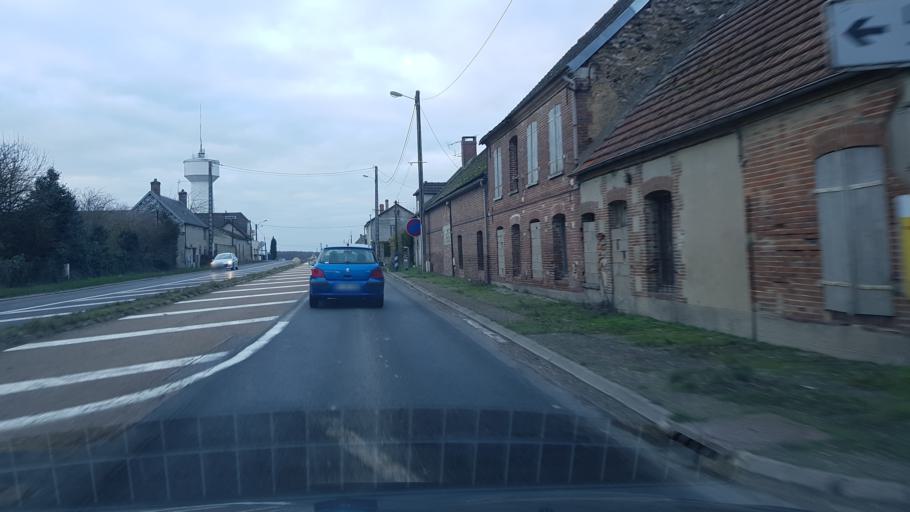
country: FR
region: Champagne-Ardenne
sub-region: Departement de la Marne
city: Esternay
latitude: 48.7317
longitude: 3.6130
